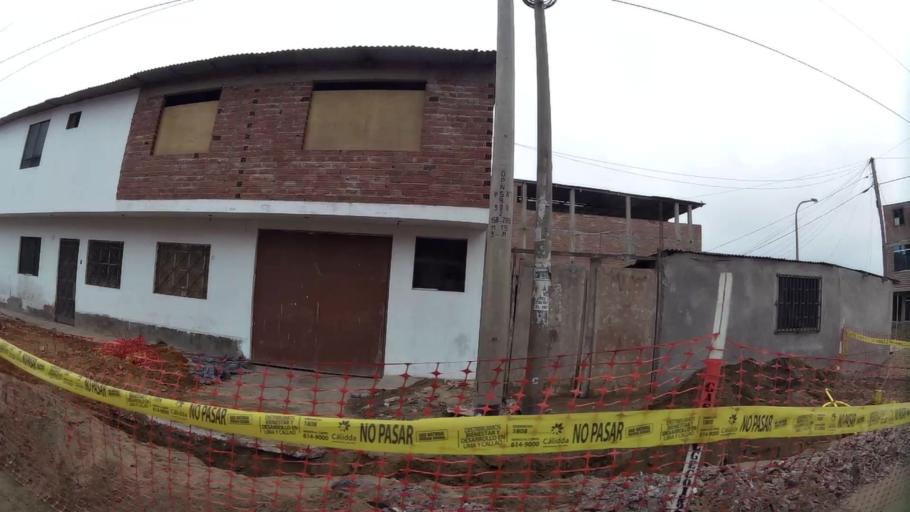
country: PE
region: Lima
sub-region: Lima
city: Punta Hermosa
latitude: -12.2364
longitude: -76.9060
